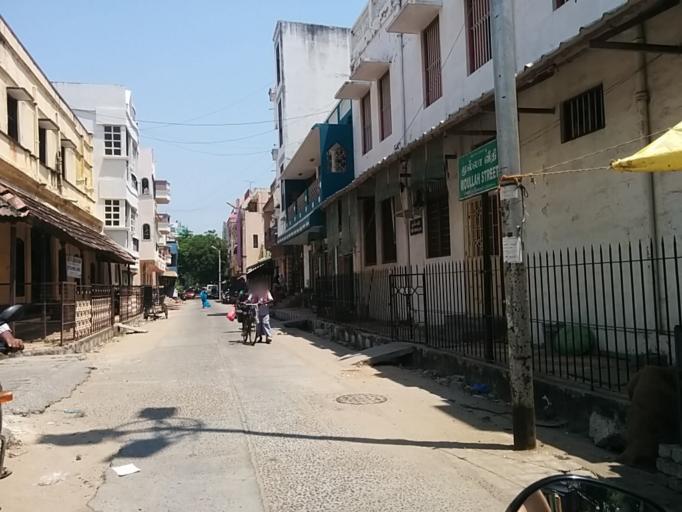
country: IN
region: Pondicherry
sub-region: Puducherry
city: Puducherry
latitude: 11.9277
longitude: 79.8301
